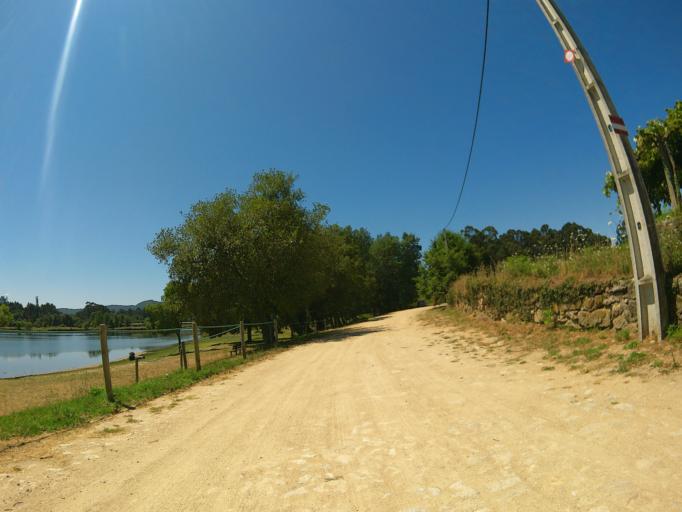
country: PT
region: Viana do Castelo
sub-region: Viana do Castelo
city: Darque
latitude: 41.7118
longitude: -8.7152
